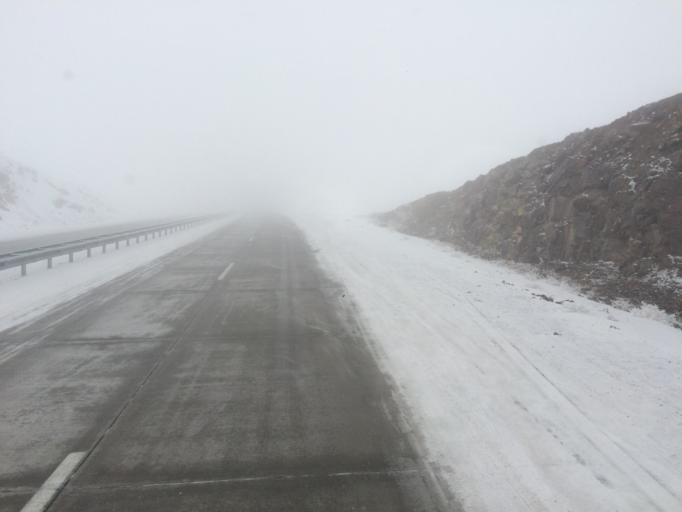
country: KZ
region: Zhambyl
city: Georgiyevka
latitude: 43.4273
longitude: 74.9585
